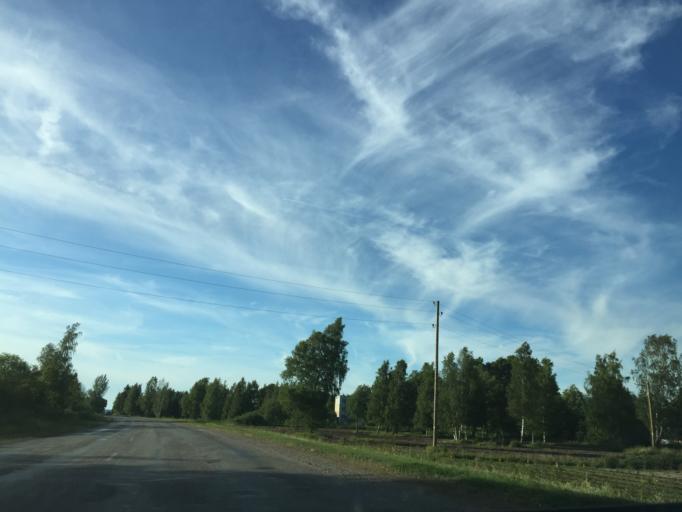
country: LV
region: Ventspils
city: Ventspils
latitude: 57.3015
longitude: 21.5612
